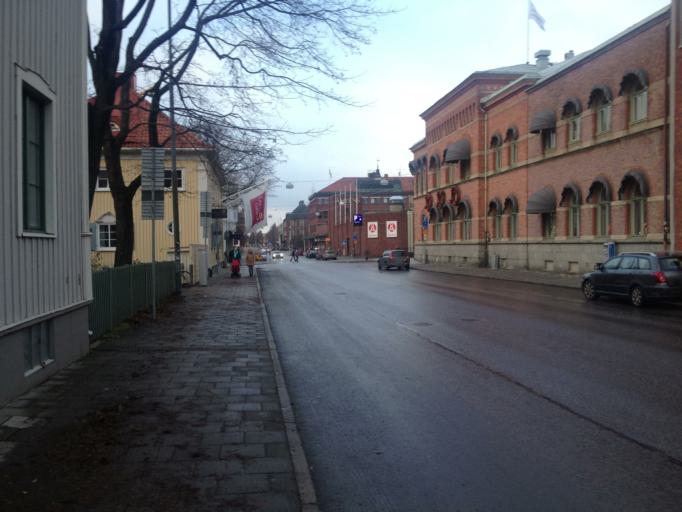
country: SE
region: Vaesterbotten
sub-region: Umea Kommun
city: Umea
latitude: 63.8242
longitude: 20.2667
